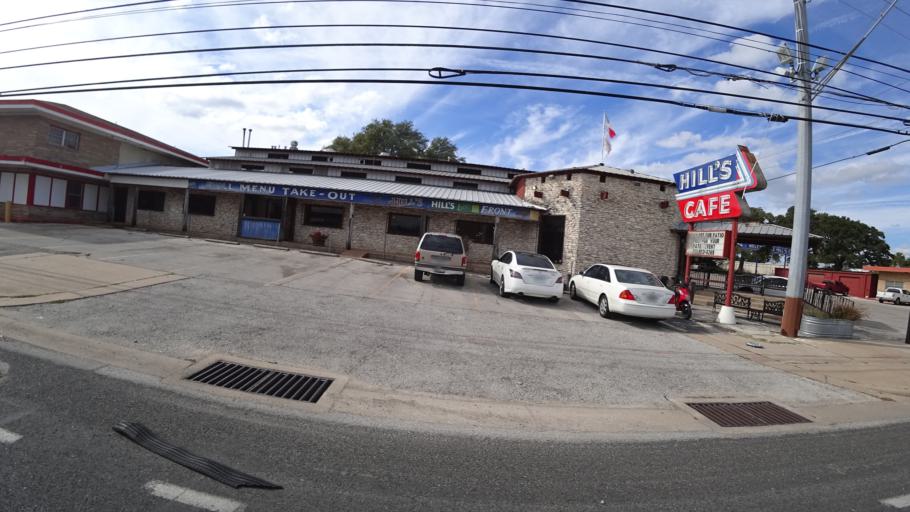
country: US
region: Texas
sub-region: Travis County
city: Austin
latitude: 30.2156
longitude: -97.7686
